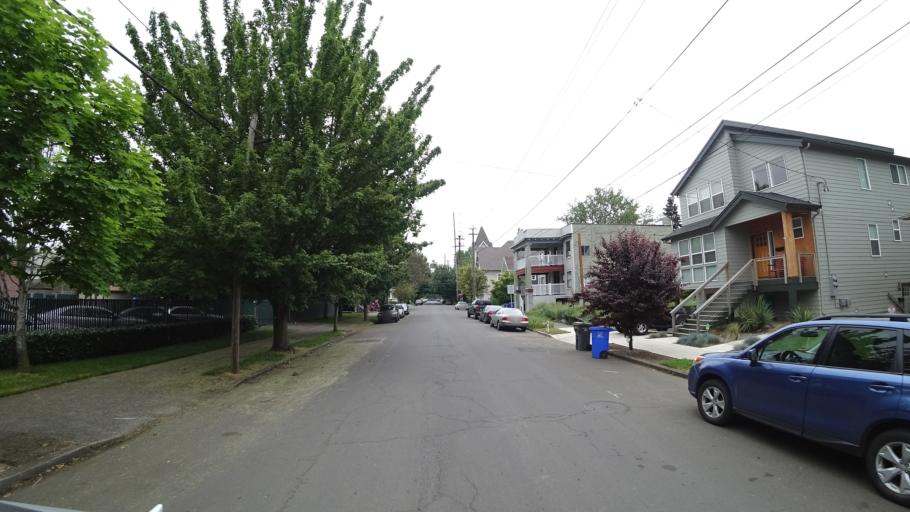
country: US
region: Oregon
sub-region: Multnomah County
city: Portland
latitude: 45.5438
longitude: -122.6653
